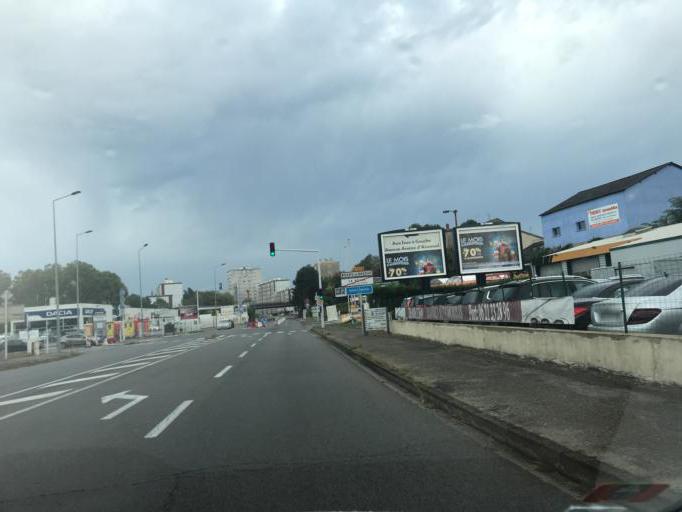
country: FR
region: Rhone-Alpes
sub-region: Departement de l'Ain
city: Bourg-en-Bresse
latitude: 46.2136
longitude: 5.2177
